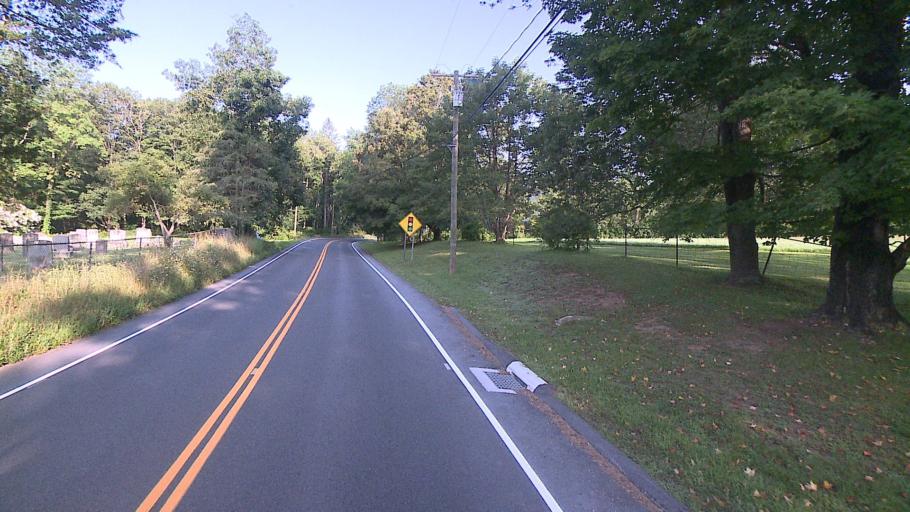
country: US
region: Connecticut
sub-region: Litchfield County
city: Kent
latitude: 41.6742
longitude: -73.5055
